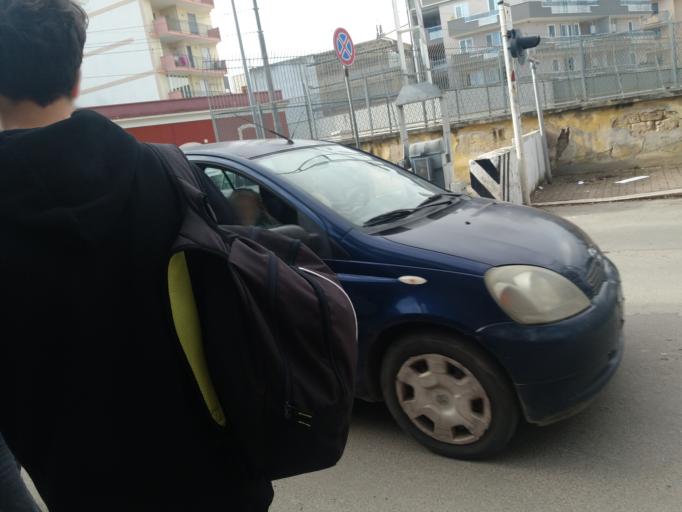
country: IT
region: Apulia
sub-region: Provincia di Barletta - Andria - Trani
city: Andria
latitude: 41.2355
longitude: 16.2947
